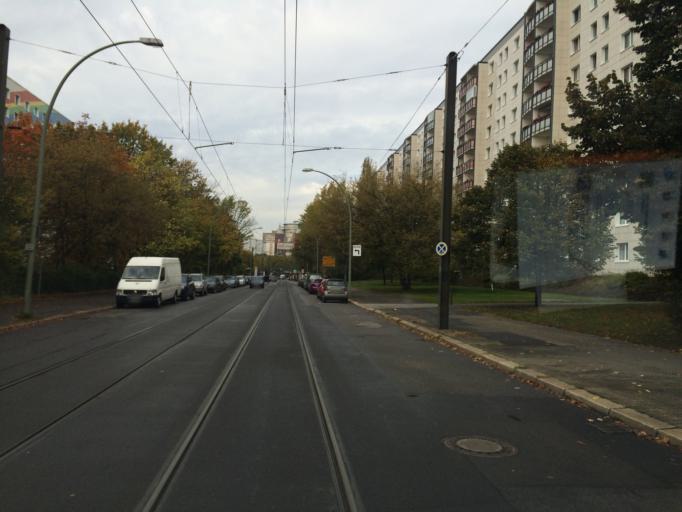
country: DE
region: Berlin
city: Fennpfuhl
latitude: 52.5267
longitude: 13.4850
